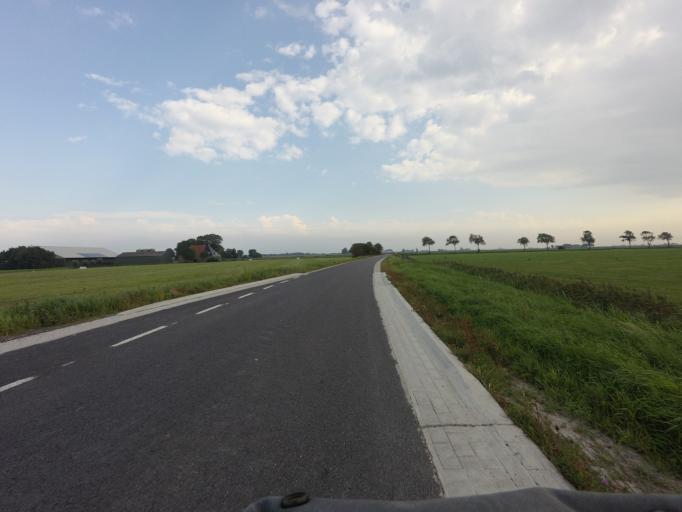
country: NL
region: Friesland
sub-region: Sudwest Fryslan
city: Bolsward
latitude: 53.0353
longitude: 5.5046
